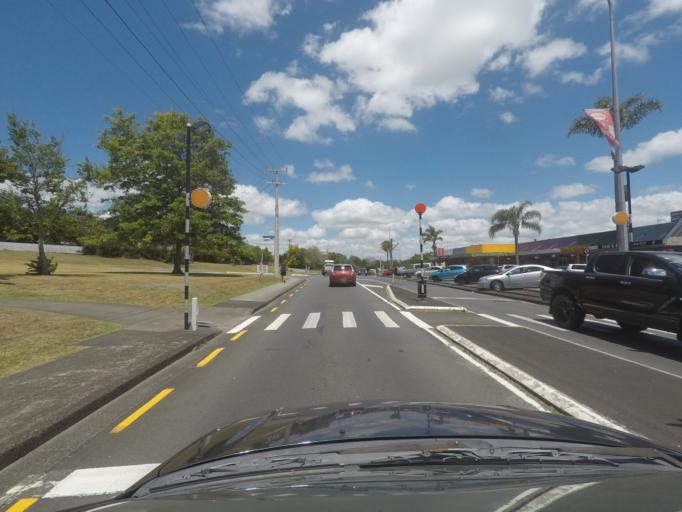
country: NZ
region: Northland
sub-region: Whangarei
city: Whangarei
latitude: -35.7547
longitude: 174.3685
